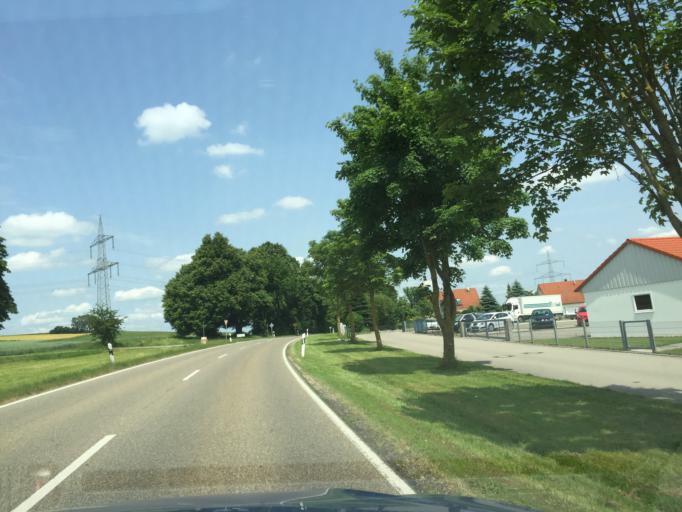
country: DE
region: Bavaria
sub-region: Swabia
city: Zusamaltheim
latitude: 48.5333
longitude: 10.6376
